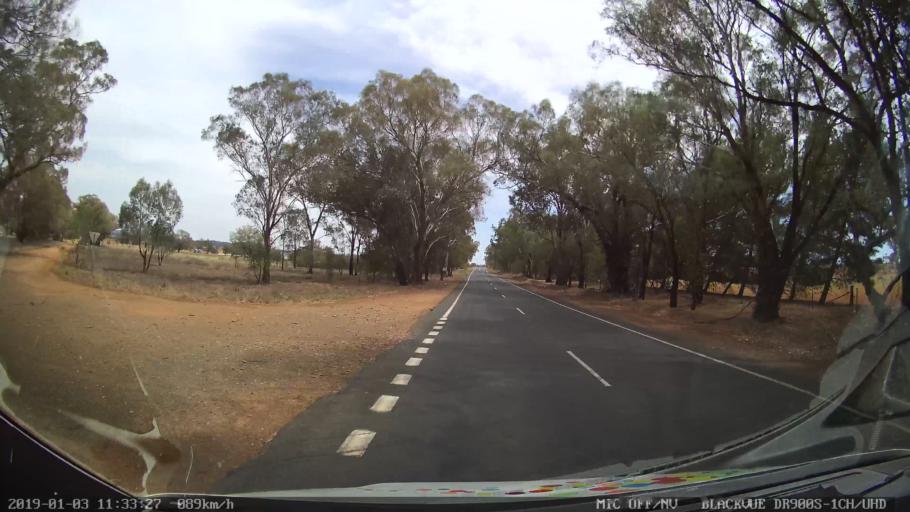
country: AU
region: New South Wales
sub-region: Weddin
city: Grenfell
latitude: -33.9467
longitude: 148.1707
